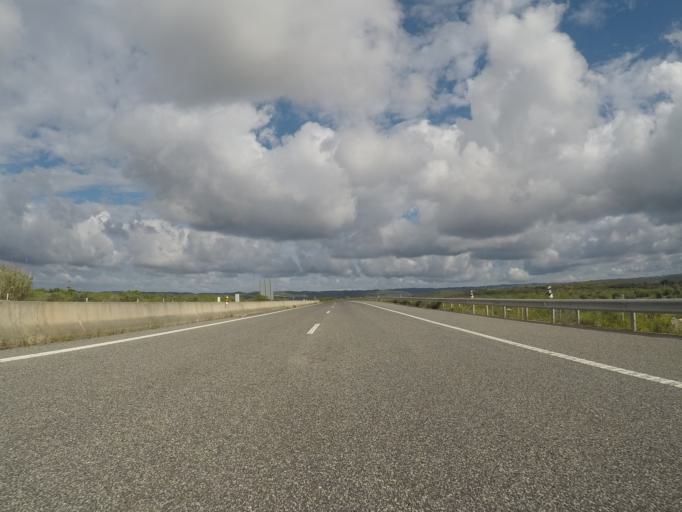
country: PT
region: Faro
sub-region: Lagos
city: Lagos
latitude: 37.1458
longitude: -8.7288
